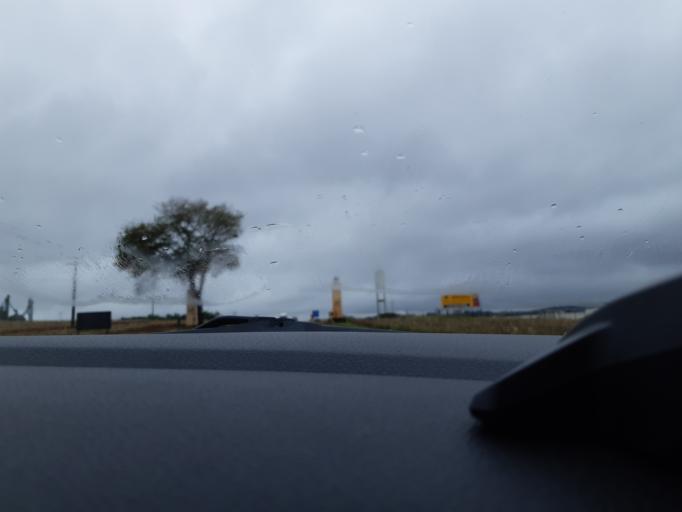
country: BR
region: Parana
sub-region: Bandeirantes
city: Bandeirantes
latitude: -23.0577
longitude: -50.2474
